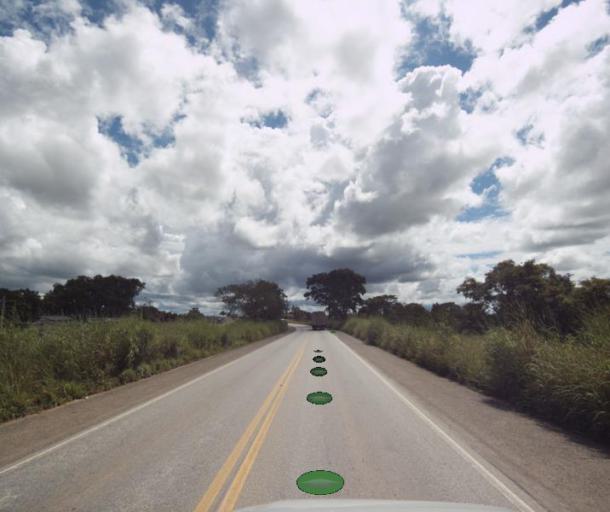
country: BR
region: Goias
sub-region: Uruacu
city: Uruacu
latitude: -14.3064
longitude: -49.1481
